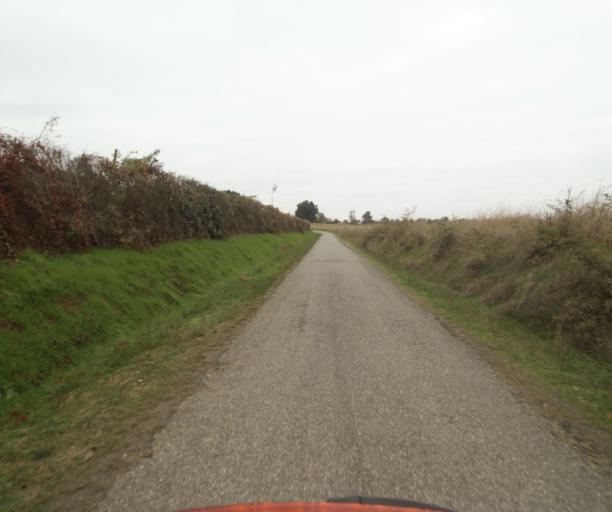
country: FR
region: Midi-Pyrenees
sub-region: Departement du Tarn-et-Garonne
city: Verdun-sur-Garonne
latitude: 43.8033
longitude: 1.2323
